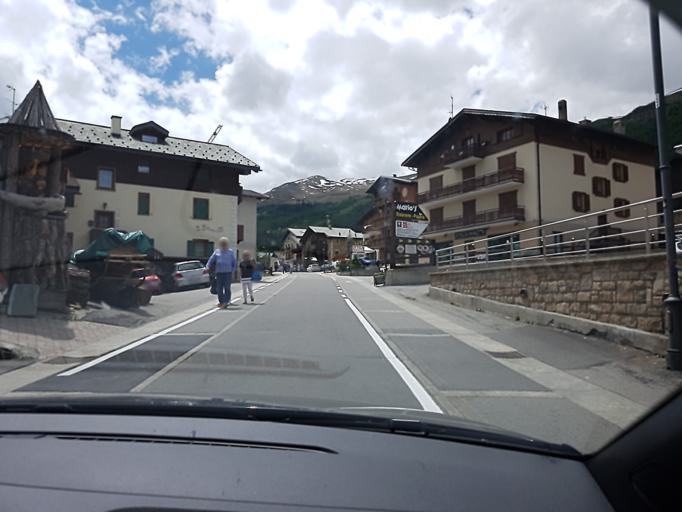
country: IT
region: Lombardy
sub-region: Provincia di Sondrio
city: Livigno
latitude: 46.5323
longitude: 10.1297
